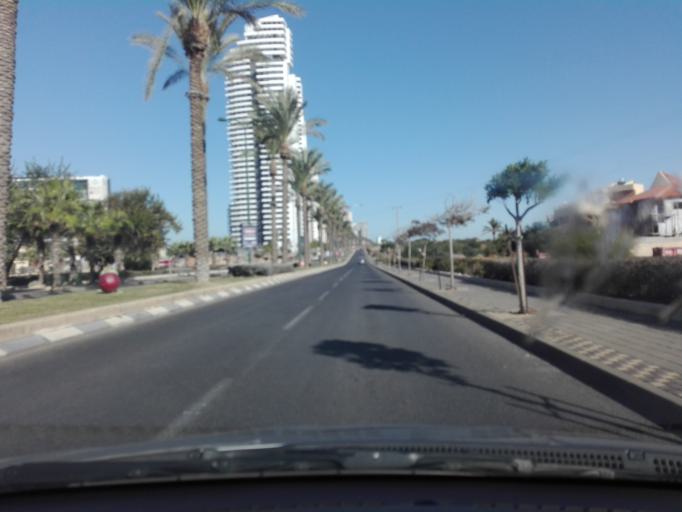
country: IL
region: Central District
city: Netanya
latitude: 32.3013
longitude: 34.8456
